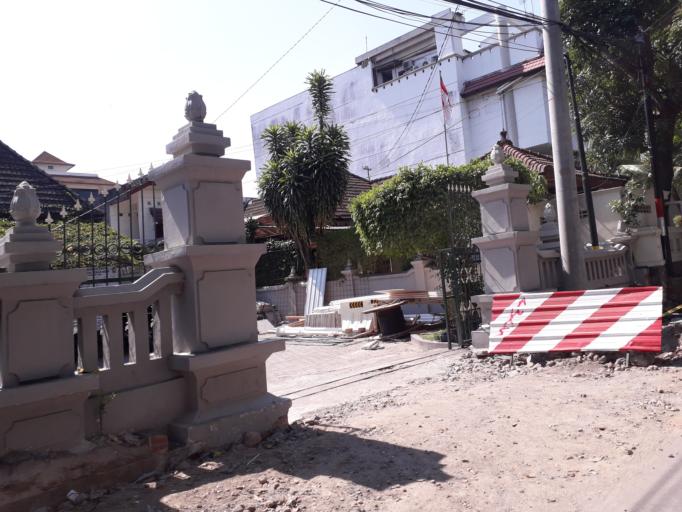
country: ID
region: Daerah Istimewa Yogyakarta
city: Yogyakarta
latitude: -7.7839
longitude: 110.3748
